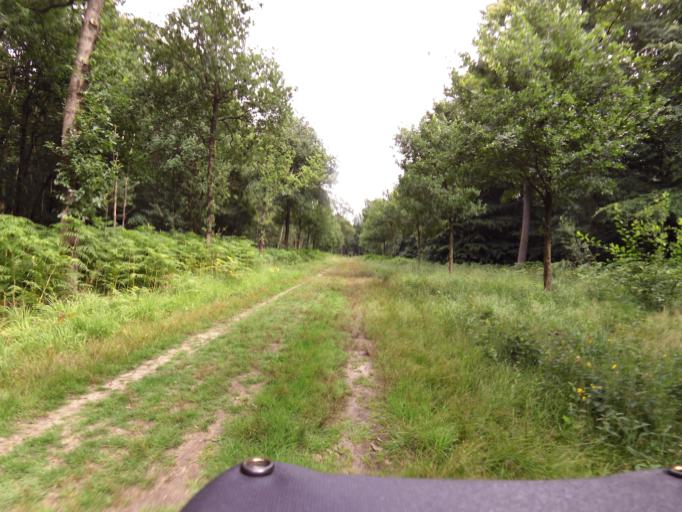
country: NL
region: North Brabant
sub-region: Gemeente Breda
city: Breda
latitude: 51.5796
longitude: 4.6939
